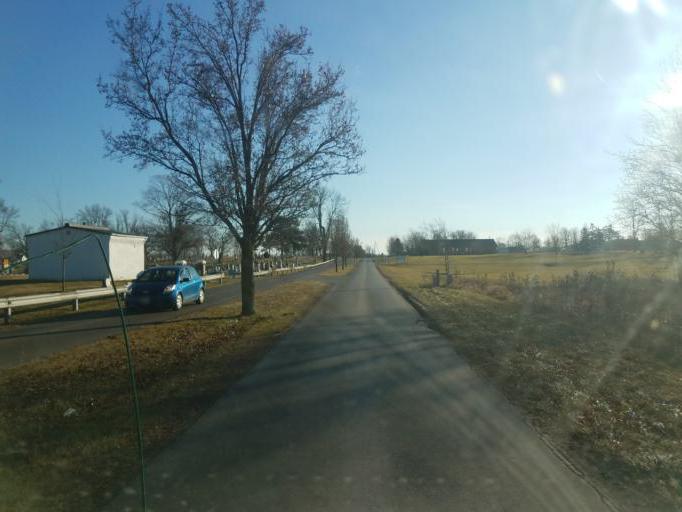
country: US
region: Ohio
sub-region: Hardin County
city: Kenton
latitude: 40.6487
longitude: -83.5905
